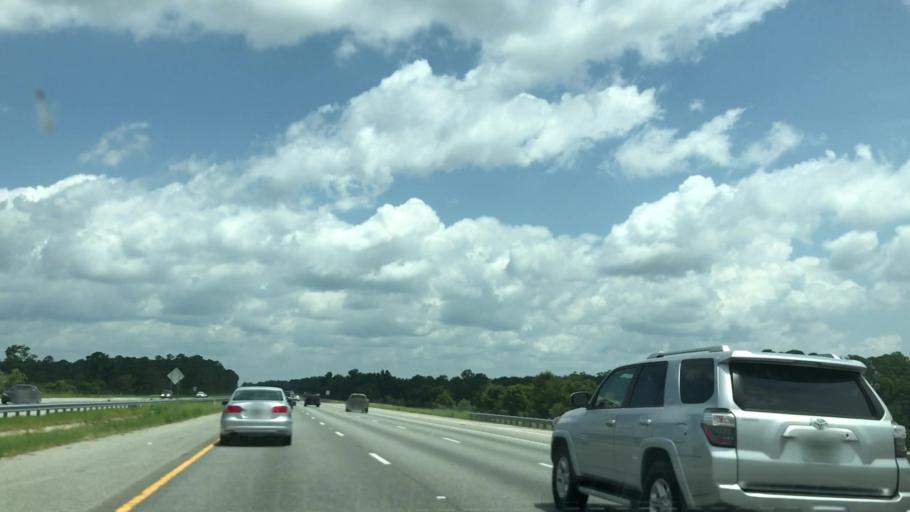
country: US
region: Georgia
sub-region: Glynn County
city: Dock Junction
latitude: 31.1690
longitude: -81.5521
